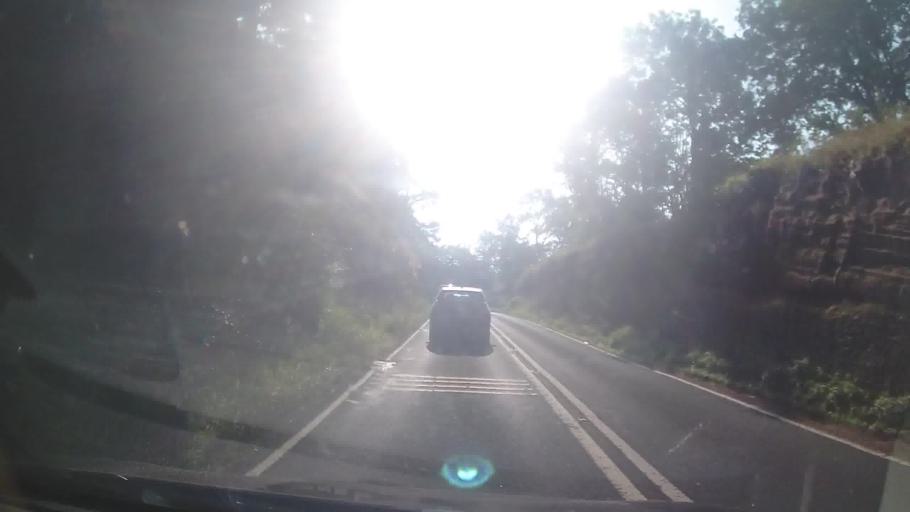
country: GB
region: England
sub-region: Shropshire
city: Bridgnorth
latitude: 52.5028
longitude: -2.3811
